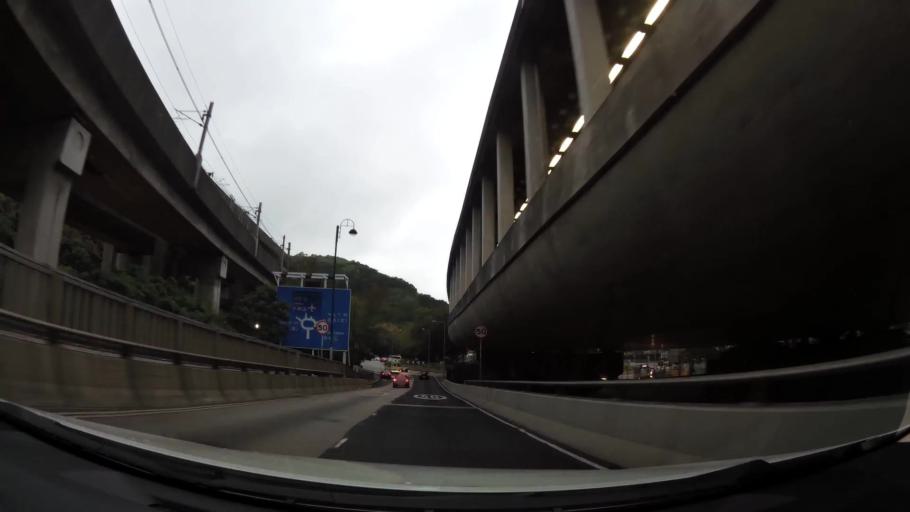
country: HK
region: Tsuen Wan
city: Tsuen Wan
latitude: 22.3591
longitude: 114.1038
